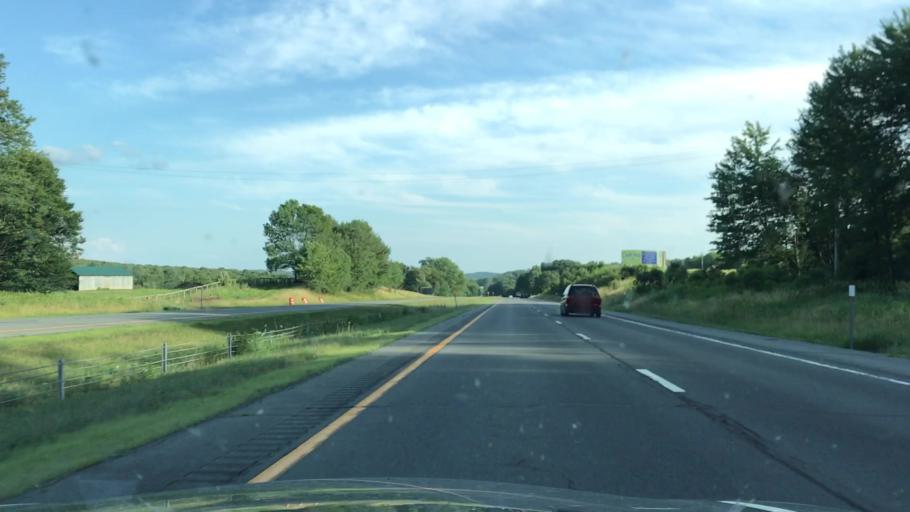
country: US
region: New York
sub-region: Sullivan County
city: Liberty
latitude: 41.7530
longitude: -74.7346
